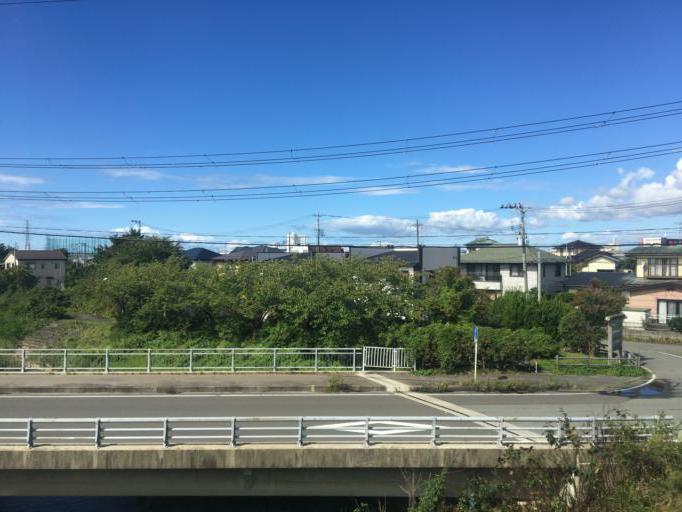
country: JP
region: Akita
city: Akita
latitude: 39.6929
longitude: 140.1110
